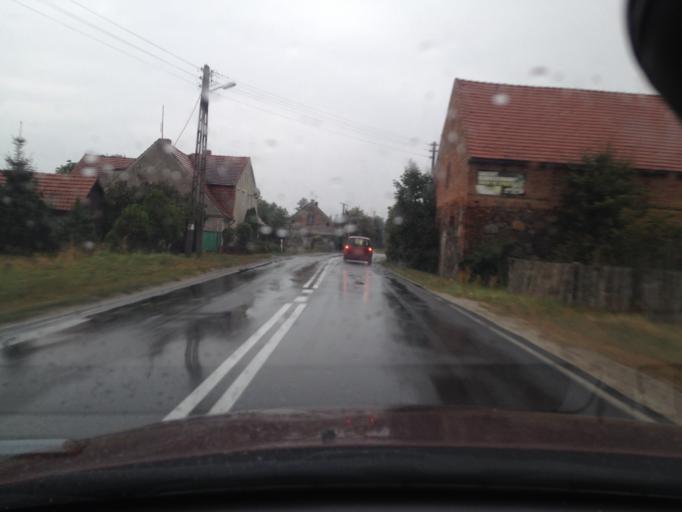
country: PL
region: Lubusz
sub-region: Powiat zaganski
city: Zagan
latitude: 51.7111
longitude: 15.2857
